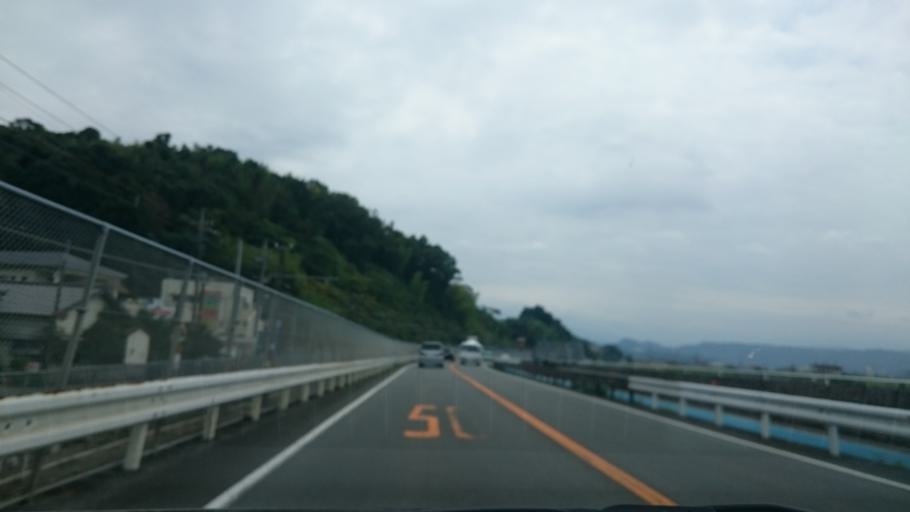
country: JP
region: Shizuoka
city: Mishima
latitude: 35.0330
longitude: 138.9492
